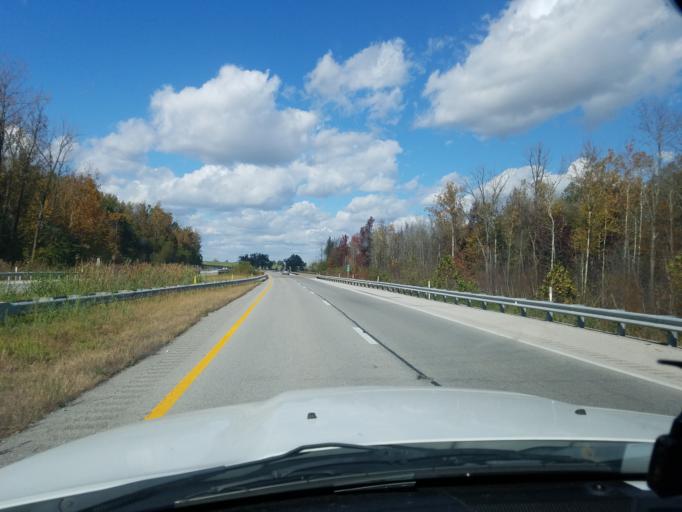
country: US
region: Kentucky
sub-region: Daviess County
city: Masonville
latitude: 37.6520
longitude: -87.0020
